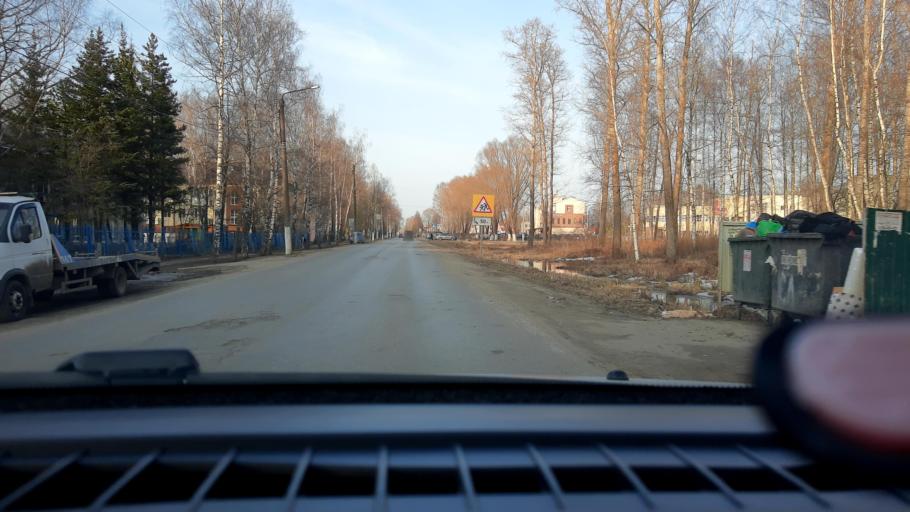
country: RU
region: Nizjnij Novgorod
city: Bogorodsk
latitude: 56.1026
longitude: 43.4814
